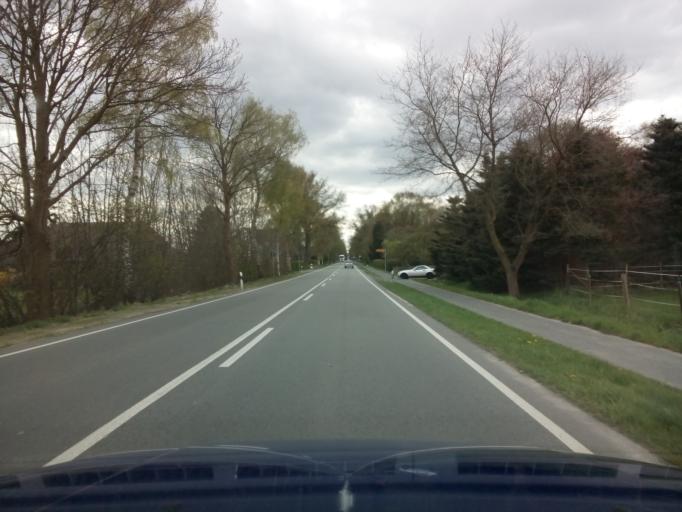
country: DE
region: Lower Saxony
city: Hambergen
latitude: 53.2976
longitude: 8.8355
